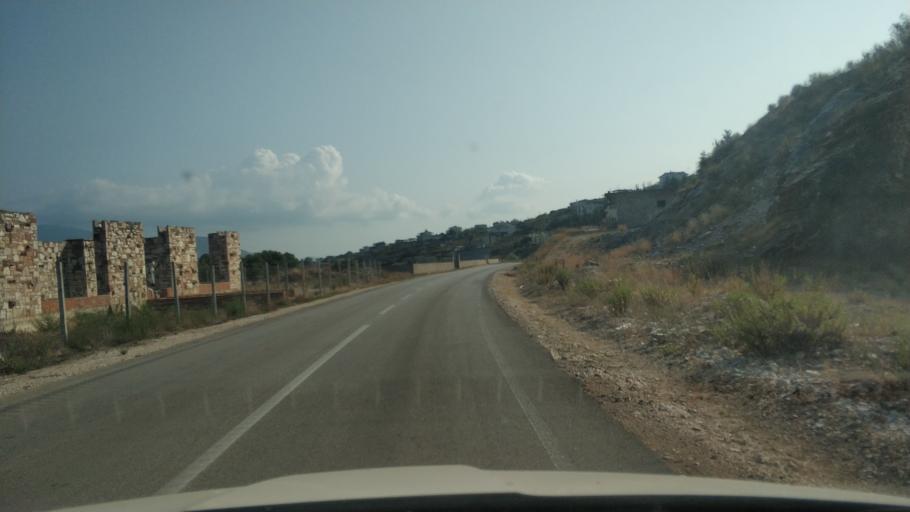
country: AL
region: Vlore
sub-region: Rrethi i Sarandes
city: Sarande
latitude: 39.8538
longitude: 20.0358
